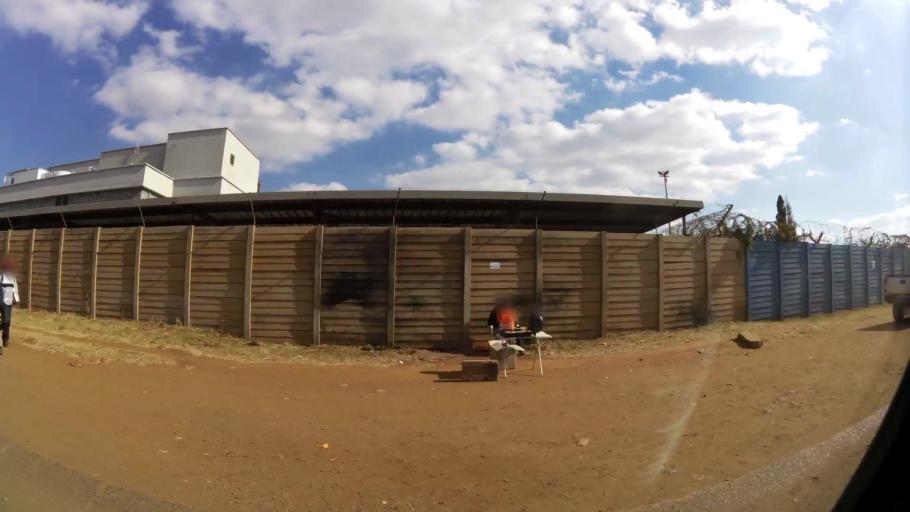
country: ZA
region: Gauteng
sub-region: Ekurhuleni Metropolitan Municipality
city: Tembisa
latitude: -25.9739
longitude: 28.2388
